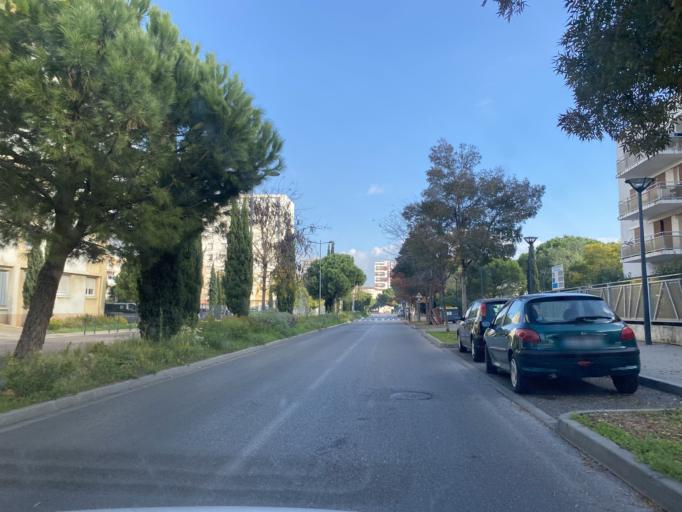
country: FR
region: Provence-Alpes-Cote d'Azur
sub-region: Departement du Var
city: La Seyne-sur-Mer
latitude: 43.1100
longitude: 5.8686
